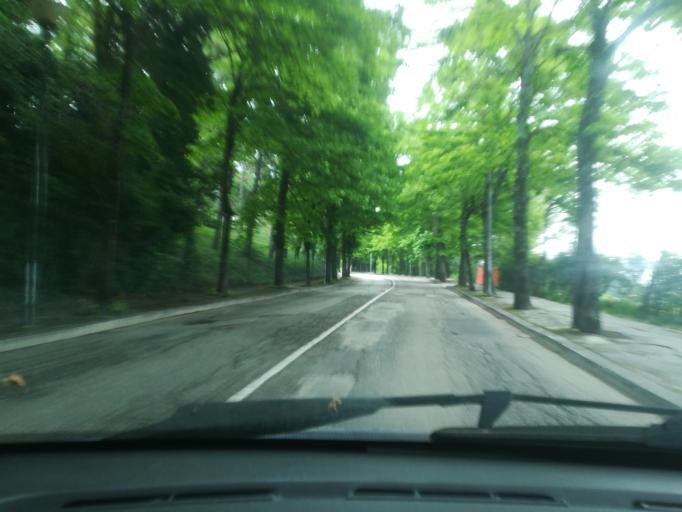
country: IT
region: The Marches
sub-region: Provincia di Macerata
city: Villa Potenza
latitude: 43.2961
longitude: 13.4255
